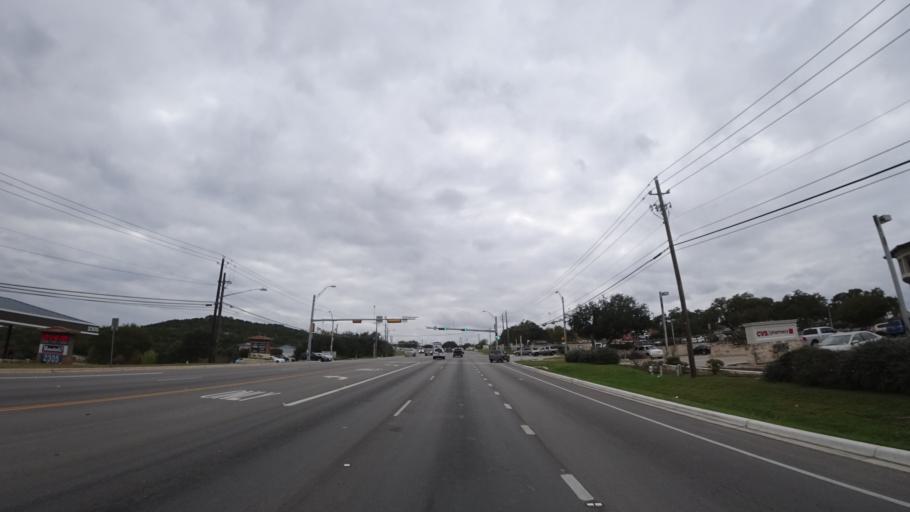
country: US
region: Texas
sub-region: Travis County
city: The Hills
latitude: 30.3415
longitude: -97.9682
